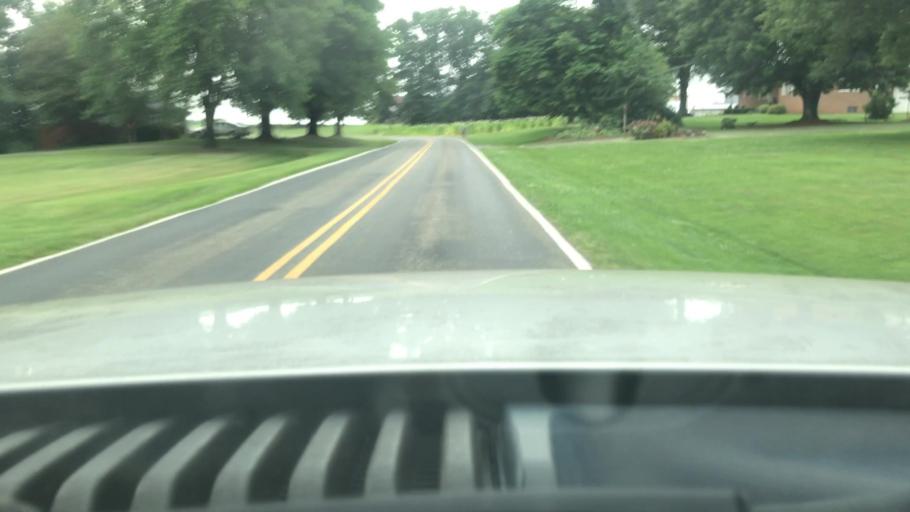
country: US
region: North Carolina
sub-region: Surry County
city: Dobson
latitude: 36.4025
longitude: -80.8043
